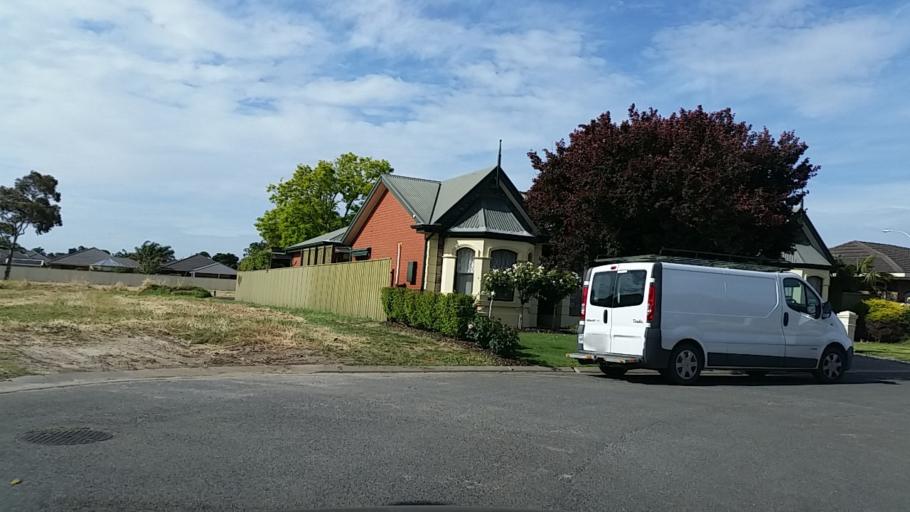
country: AU
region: South Australia
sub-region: Charles Sturt
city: Grange
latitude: -34.8928
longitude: 138.4992
